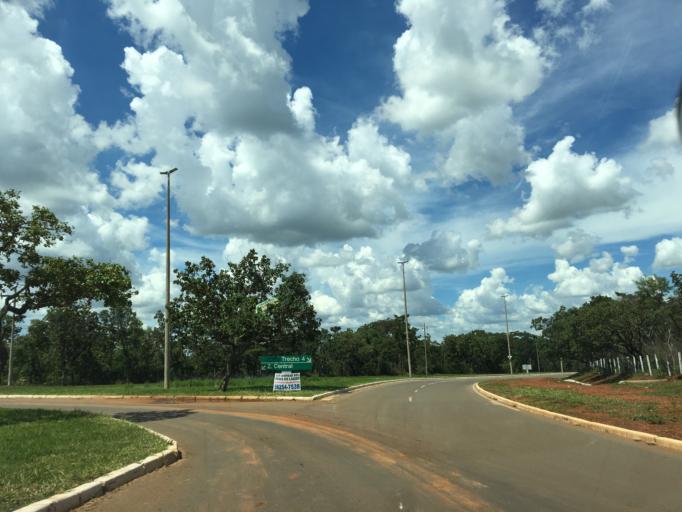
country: BR
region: Federal District
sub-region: Brasilia
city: Brasilia
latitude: -15.8068
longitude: -47.8379
